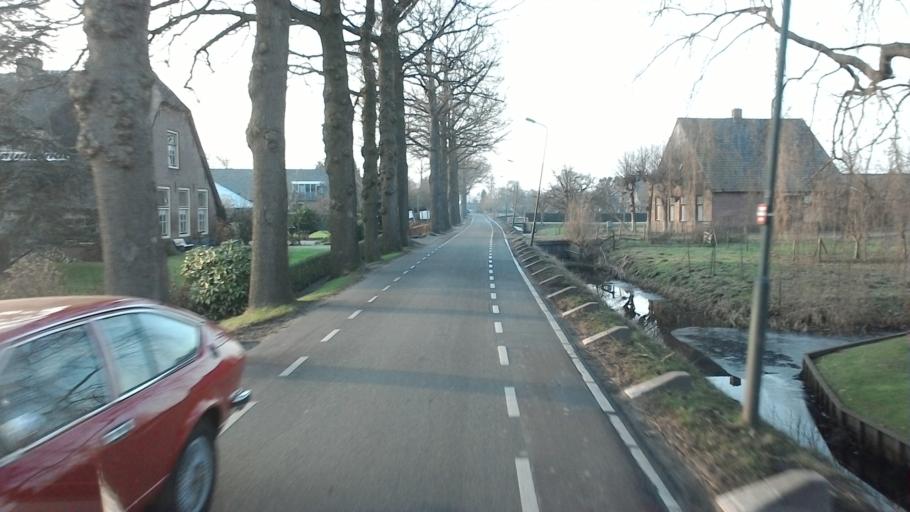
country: NL
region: Utrecht
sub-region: Gemeente De Bilt
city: De Bilt
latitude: 52.1496
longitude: 5.1555
